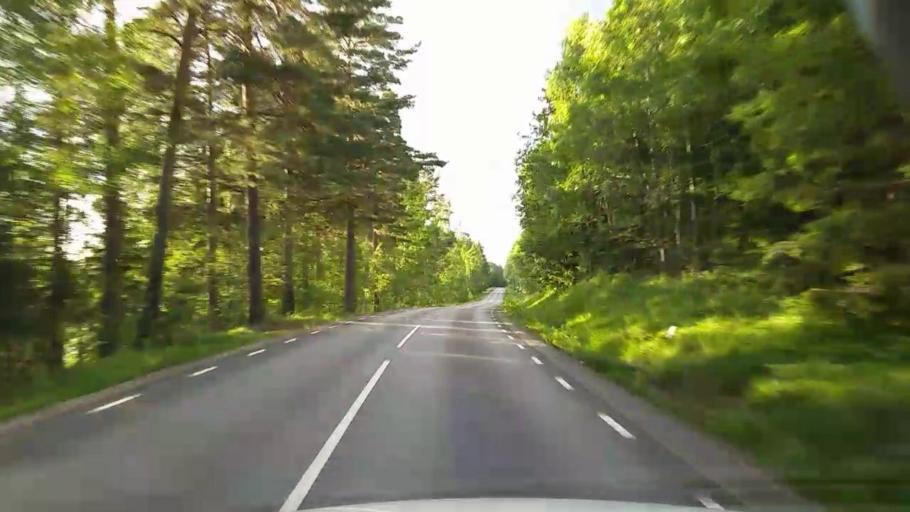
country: SE
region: Vaestmanland
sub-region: Kopings Kommun
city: Kolsva
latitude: 59.7313
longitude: 15.8262
